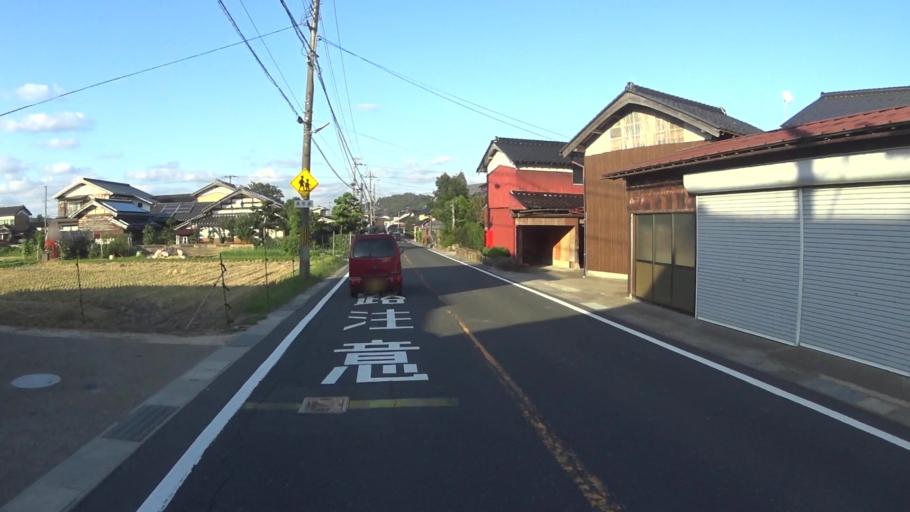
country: JP
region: Kyoto
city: Miyazu
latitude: 35.5903
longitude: 135.0392
